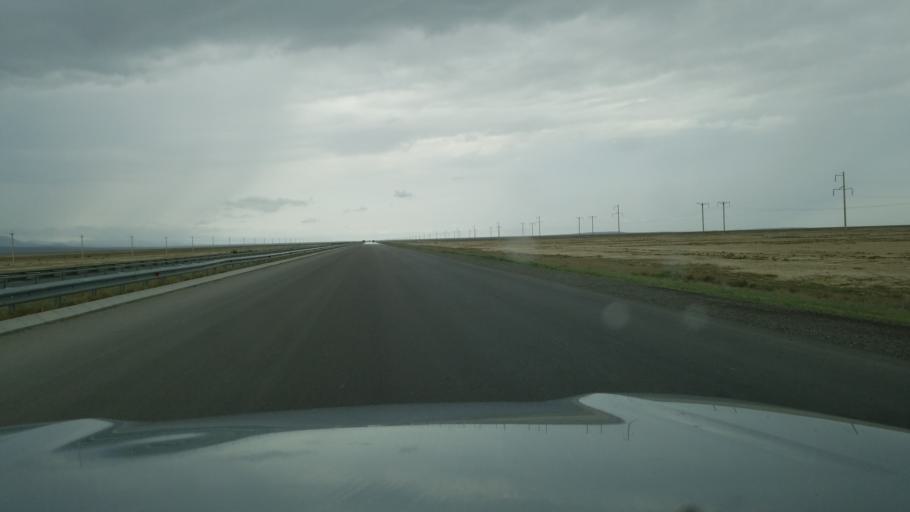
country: TM
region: Balkan
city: Serdar
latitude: 39.0482
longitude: 56.1354
